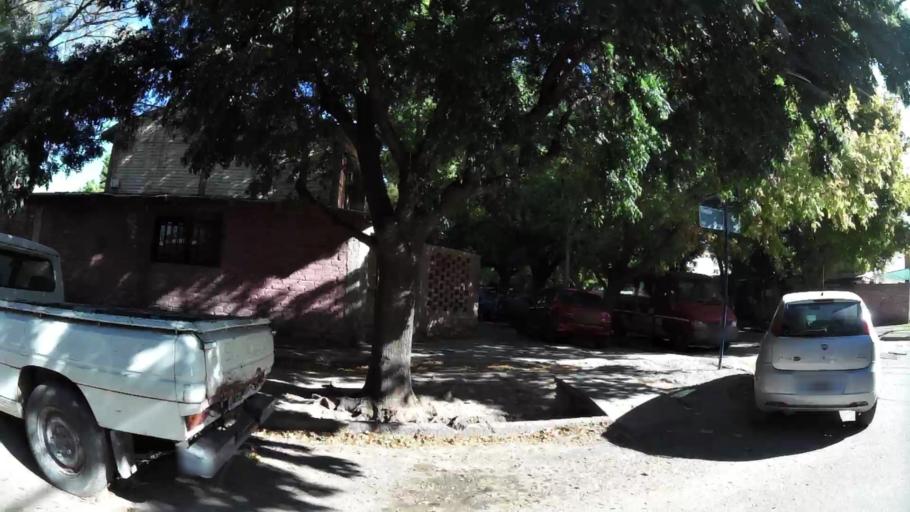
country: AR
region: Mendoza
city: Las Heras
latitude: -32.8514
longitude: -68.8289
